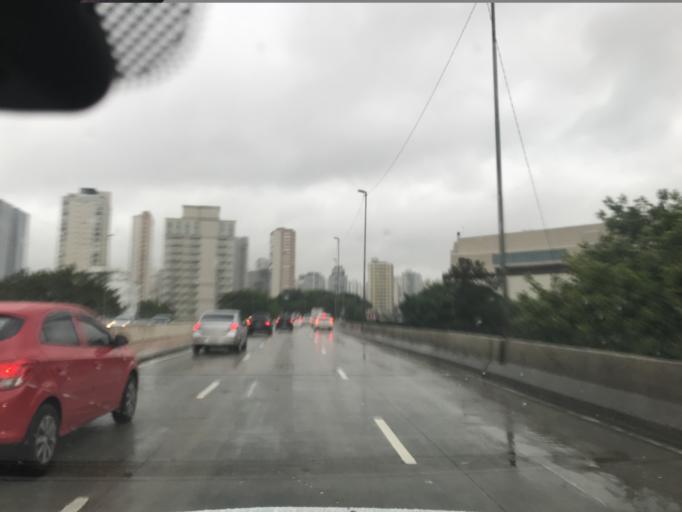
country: BR
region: Sao Paulo
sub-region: Sao Paulo
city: Sao Paulo
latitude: -23.5259
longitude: -46.6720
